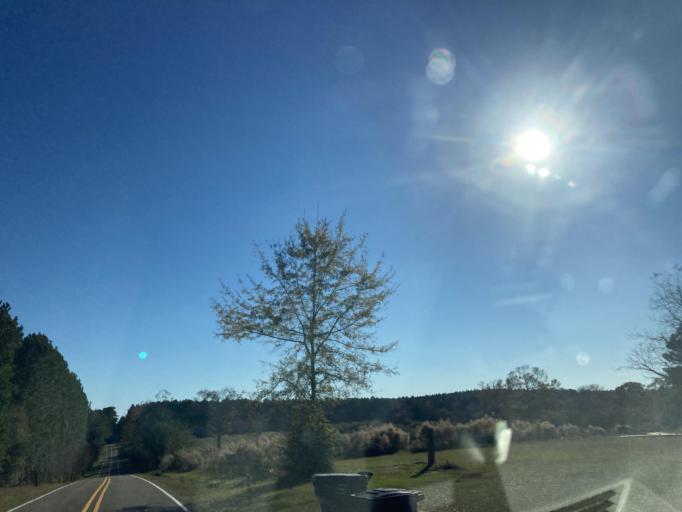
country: US
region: Mississippi
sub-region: Lamar County
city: Sumrall
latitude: 31.3653
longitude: -89.5694
